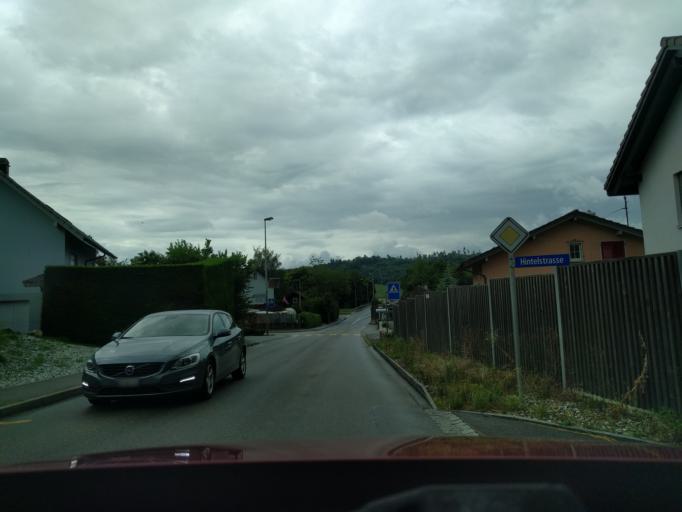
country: CH
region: Bern
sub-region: Bern-Mittelland District
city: Munchenbuchsee
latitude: 47.0400
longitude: 7.4302
